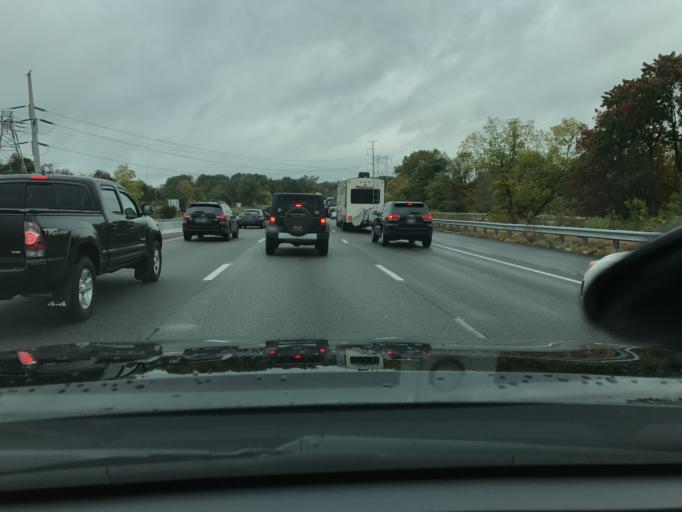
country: US
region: Massachusetts
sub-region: Essex County
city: Lynnfield
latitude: 42.5133
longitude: -71.0421
